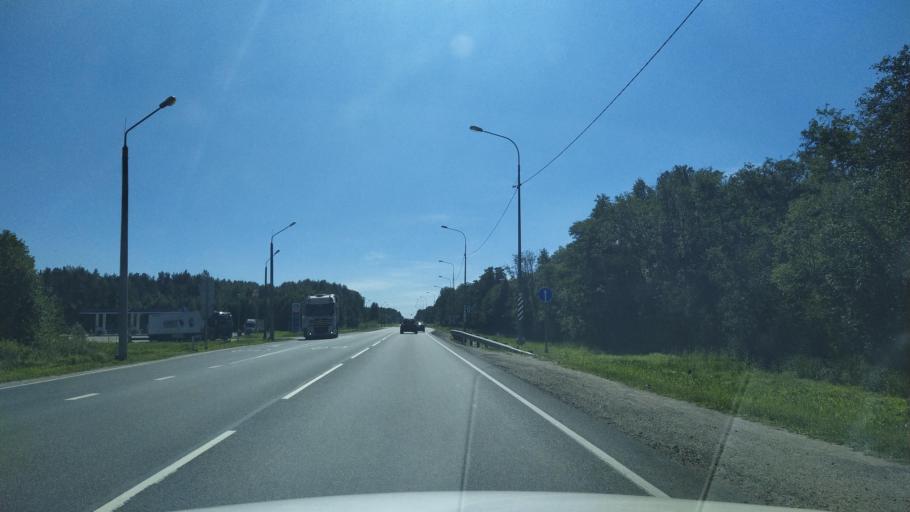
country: RU
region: Pskov
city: Pskov
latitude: 57.7838
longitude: 28.4067
